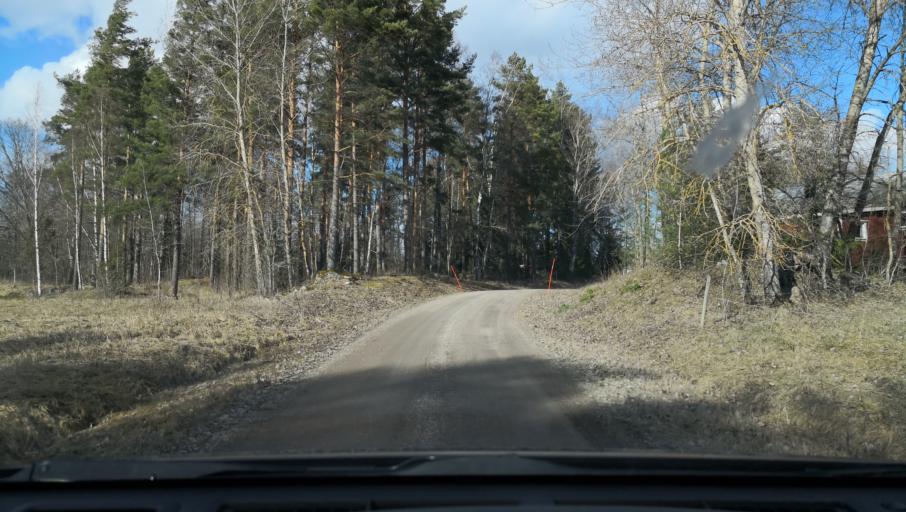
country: SE
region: OErebro
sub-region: Lindesbergs Kommun
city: Fellingsbro
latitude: 59.4308
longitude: 15.6859
